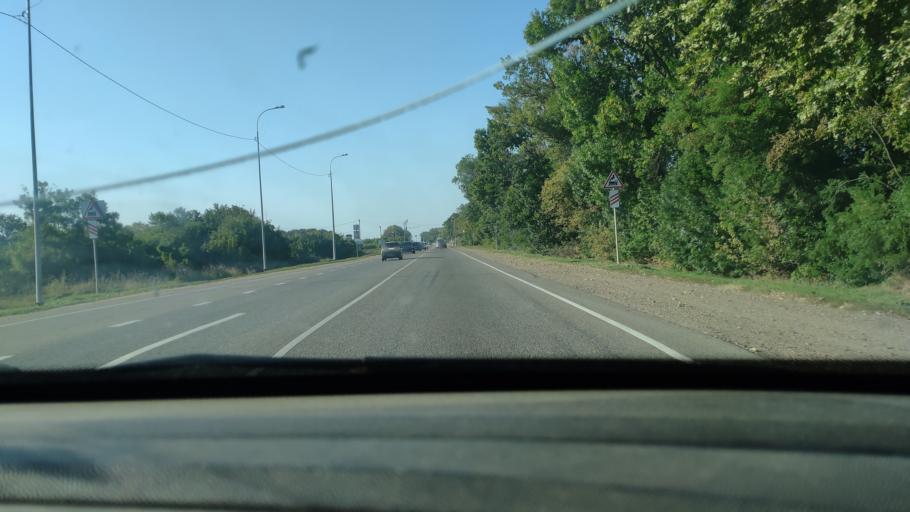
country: RU
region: Krasnodarskiy
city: Medvedovskaya
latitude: 45.4464
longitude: 38.9937
